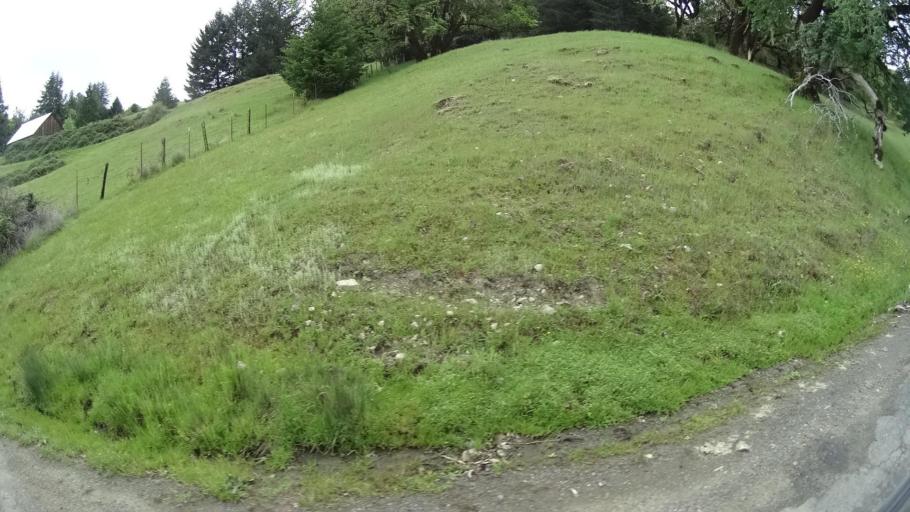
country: US
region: California
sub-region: Humboldt County
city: Redway
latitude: 40.1731
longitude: -123.5703
